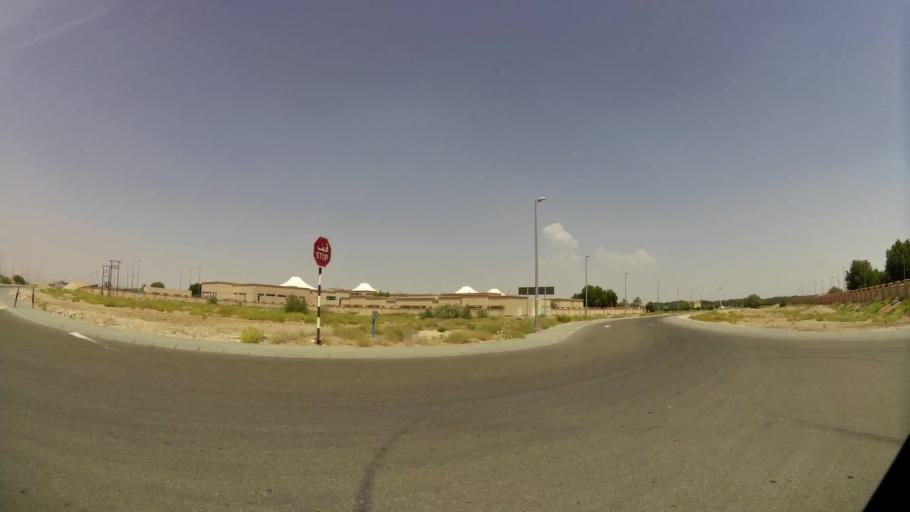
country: AE
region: Abu Dhabi
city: Al Ain
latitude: 24.2592
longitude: 55.6890
